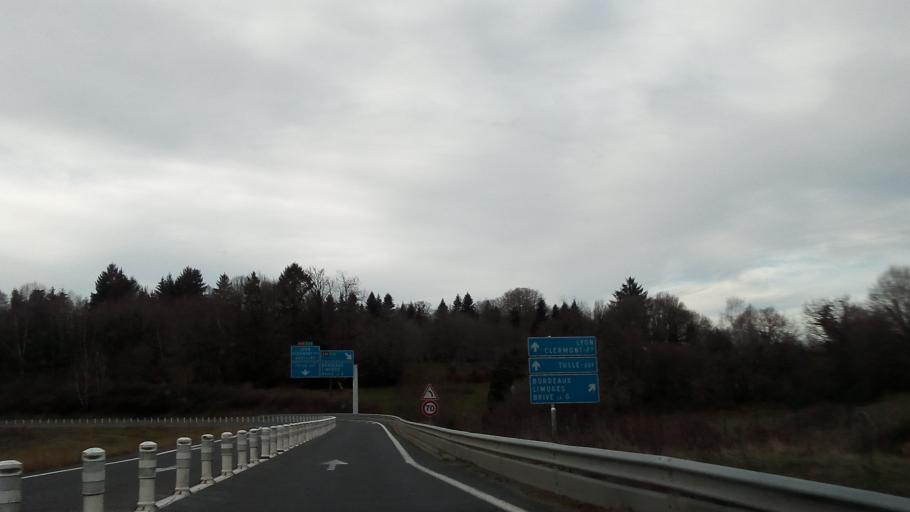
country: FR
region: Limousin
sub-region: Departement de la Correze
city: Naves
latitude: 45.3297
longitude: 1.7622
